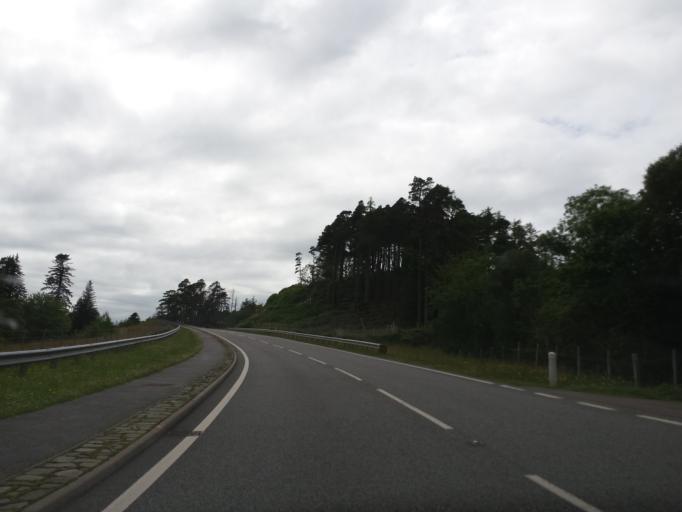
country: GB
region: Scotland
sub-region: Argyll and Bute
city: Isle Of Mull
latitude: 56.9000
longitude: -5.7888
